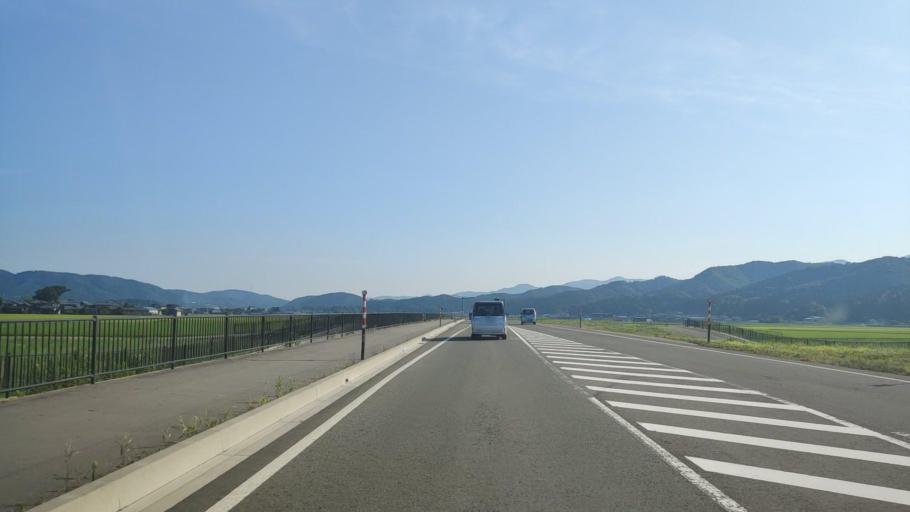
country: JP
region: Fukui
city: Maruoka
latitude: 36.1770
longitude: 136.2661
